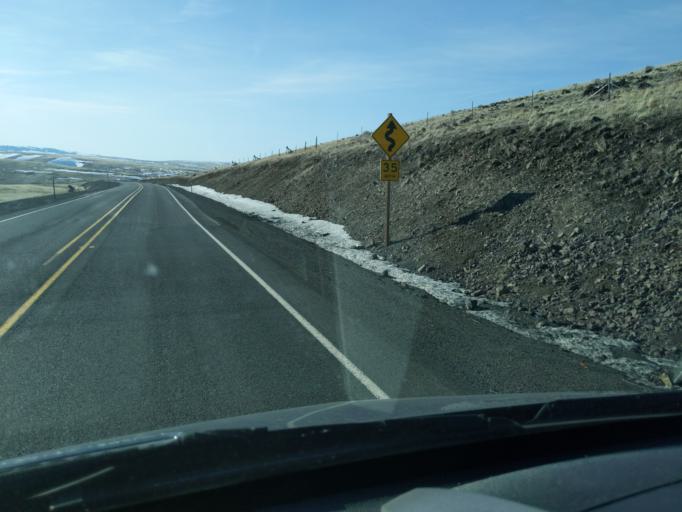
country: US
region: Oregon
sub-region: Umatilla County
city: Pilot Rock
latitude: 45.2999
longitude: -119.0009
